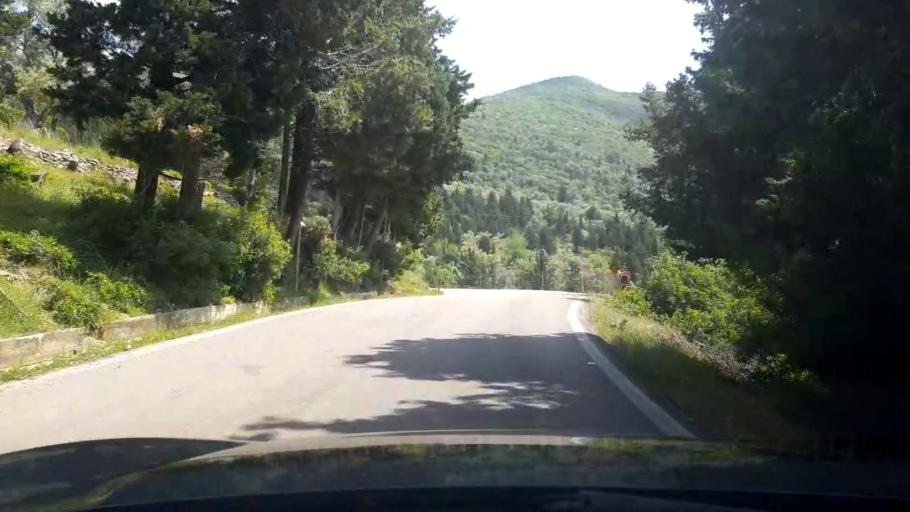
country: GR
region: Ionian Islands
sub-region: Lefkada
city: Nidri
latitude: 38.6527
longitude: 20.7058
